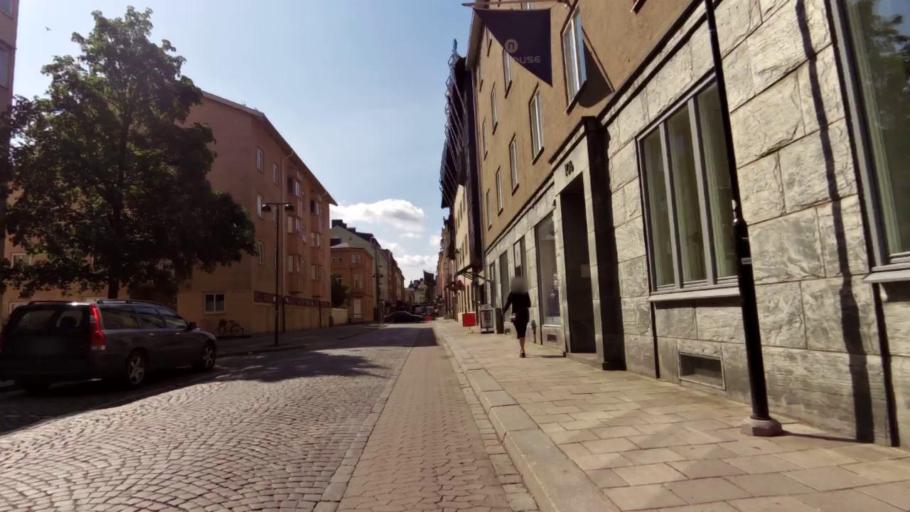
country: SE
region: OEstergoetland
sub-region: Linkopings Kommun
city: Linkoping
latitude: 58.4134
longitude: 15.6199
